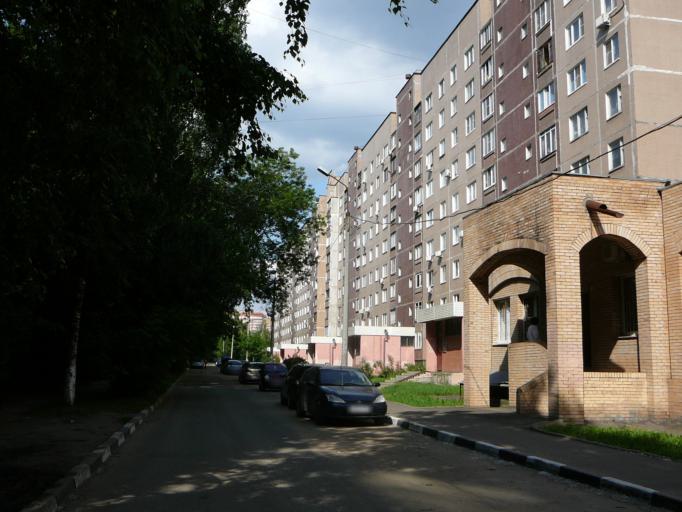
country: RU
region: Moskovskaya
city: Krasnogorsk
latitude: 55.8147
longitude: 37.3218
